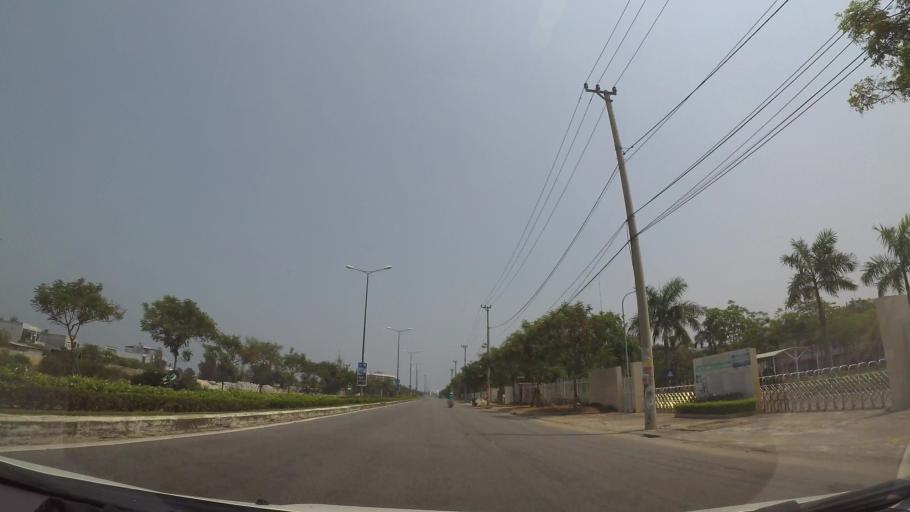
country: VN
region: Da Nang
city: Ngu Hanh Son
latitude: 15.9779
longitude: 108.2574
